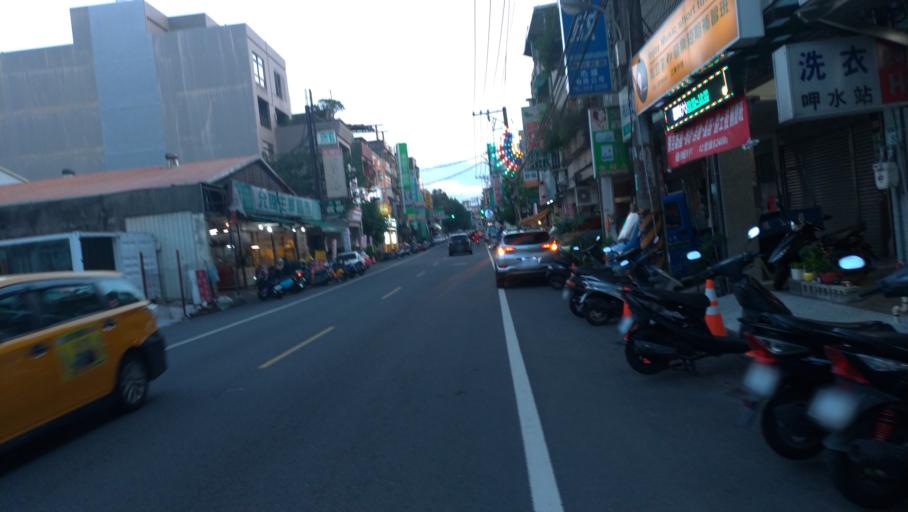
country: TW
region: Taiwan
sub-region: Taoyuan
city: Taoyuan
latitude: 24.9850
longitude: 121.3144
